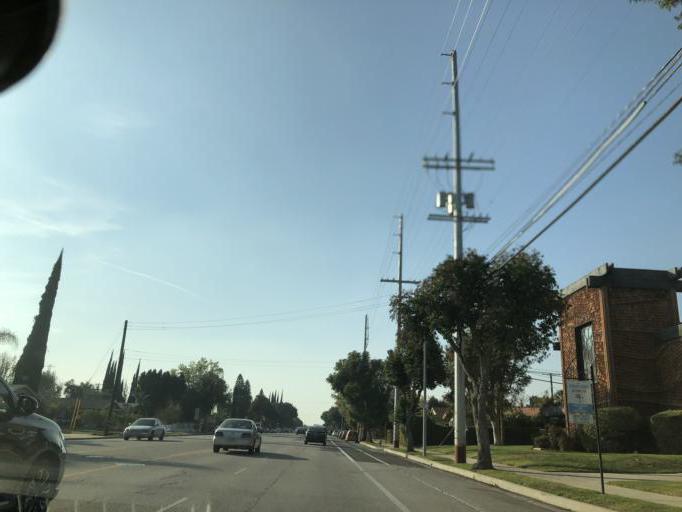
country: US
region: California
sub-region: Los Angeles County
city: San Fernando
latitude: 34.2793
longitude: -118.4950
